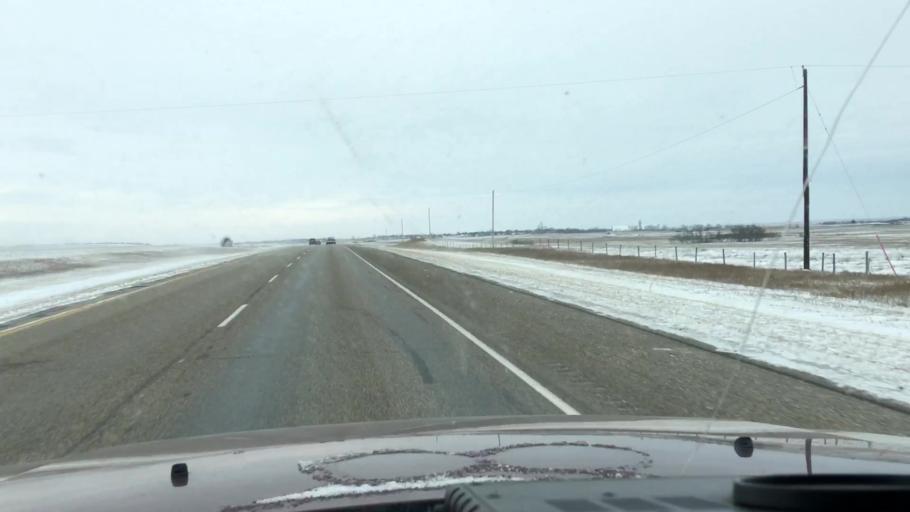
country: CA
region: Saskatchewan
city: Saskatoon
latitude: 51.6564
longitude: -106.4427
